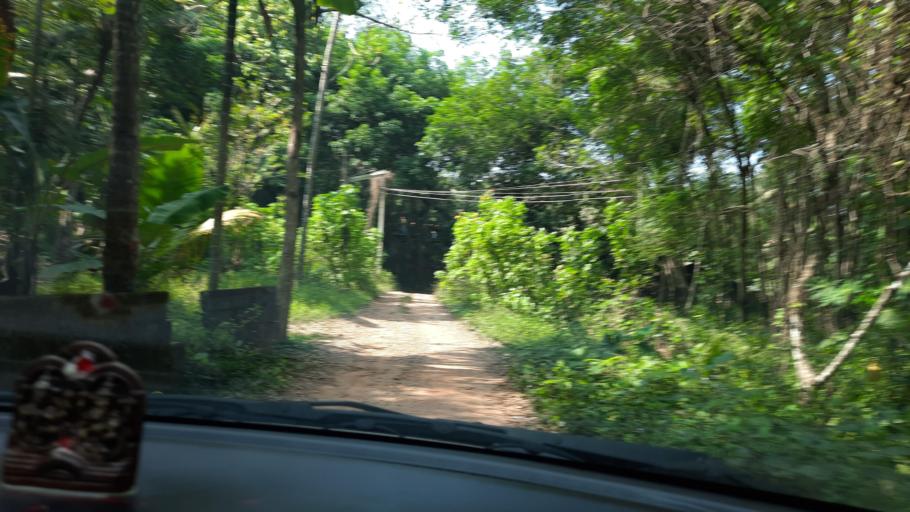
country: IN
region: Kerala
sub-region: Thiruvananthapuram
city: Nedumangad
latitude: 8.5921
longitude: 76.9258
